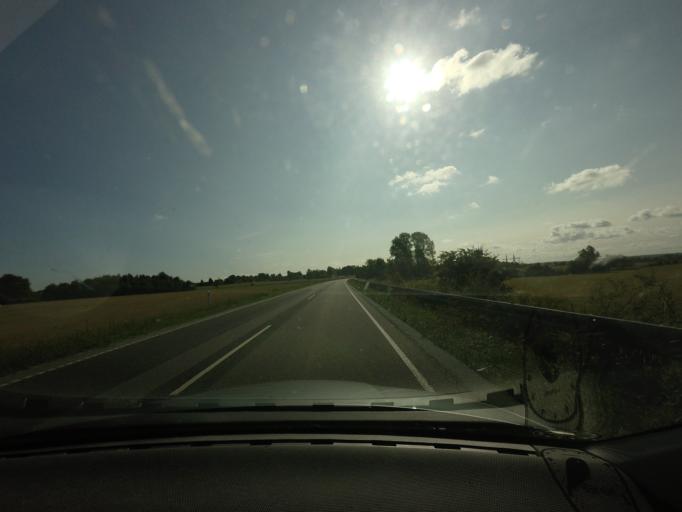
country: DK
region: Zealand
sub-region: Vordingborg Kommune
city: Praesto
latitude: 55.0095
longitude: 12.1333
